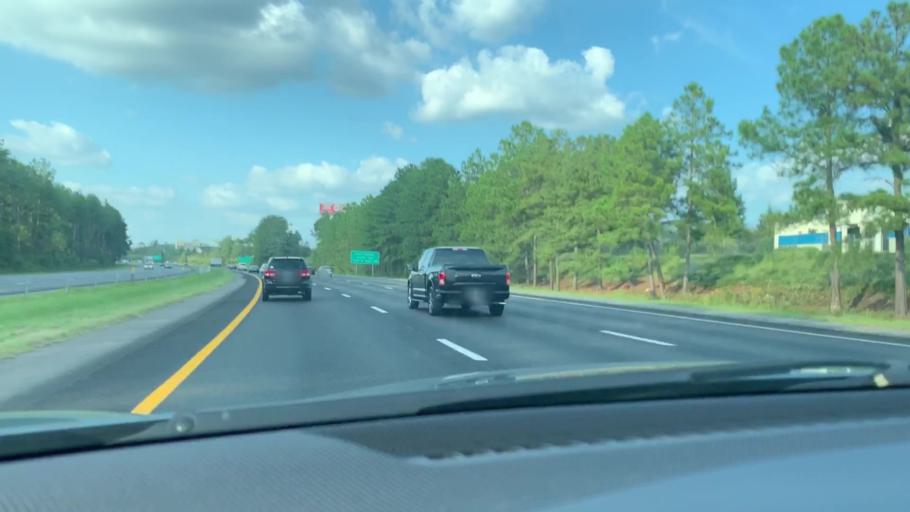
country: US
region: South Carolina
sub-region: Richland County
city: Forest Acres
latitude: 33.9603
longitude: -80.9533
